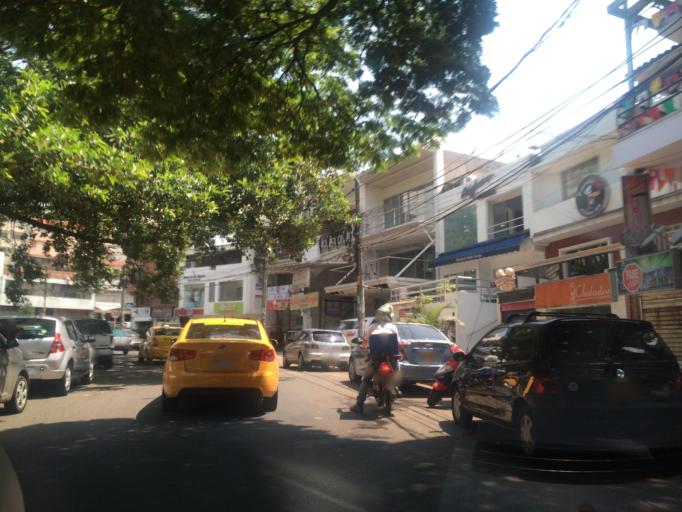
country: CO
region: Valle del Cauca
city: Cali
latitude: 3.4360
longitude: -76.5450
